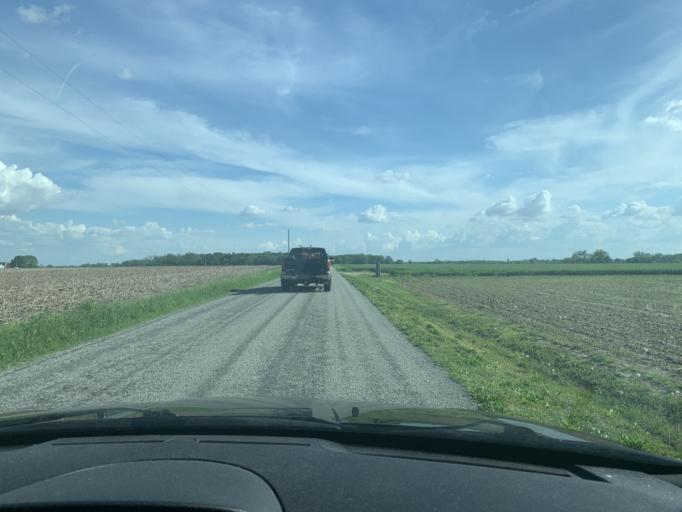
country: US
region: Ohio
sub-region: Logan County
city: De Graff
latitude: 40.2483
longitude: -84.0172
